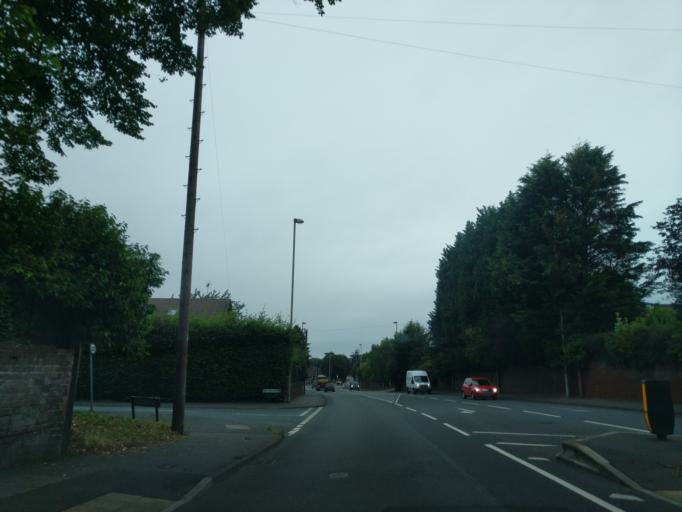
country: GB
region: England
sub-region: Worcestershire
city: Hagley
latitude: 52.4356
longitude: -2.1324
